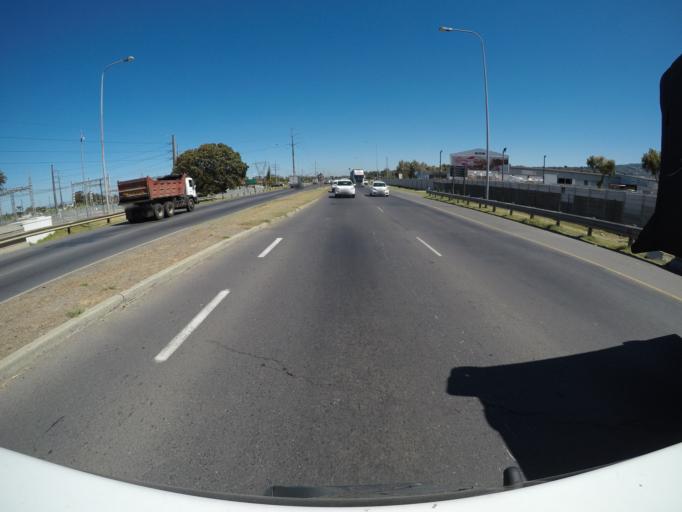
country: ZA
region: Western Cape
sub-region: Cape Winelands District Municipality
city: Stellenbosch
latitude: -34.0907
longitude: 18.8410
